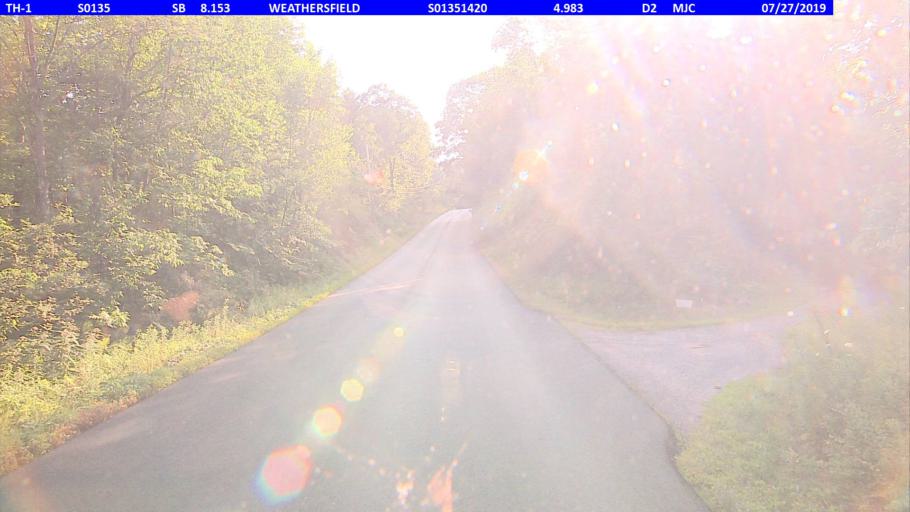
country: US
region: Vermont
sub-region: Windsor County
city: Windsor
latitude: 43.4092
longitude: -72.4555
